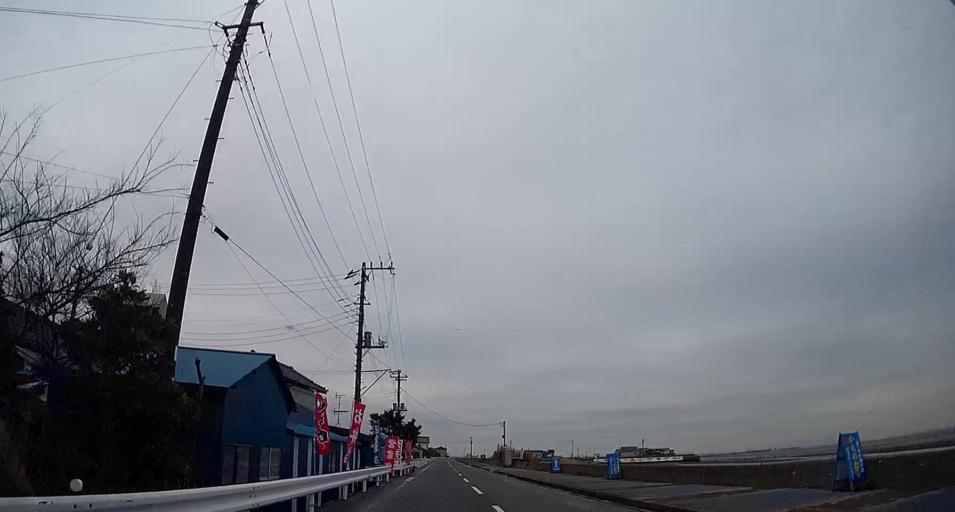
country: JP
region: Chiba
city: Kisarazu
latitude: 35.4326
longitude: 139.9090
